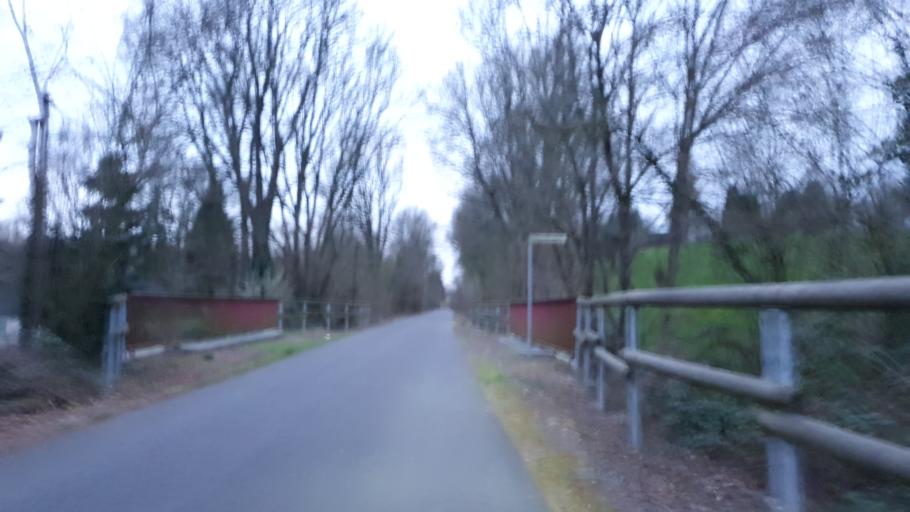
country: DE
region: North Rhine-Westphalia
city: Opladen
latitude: 51.0753
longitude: 7.0360
